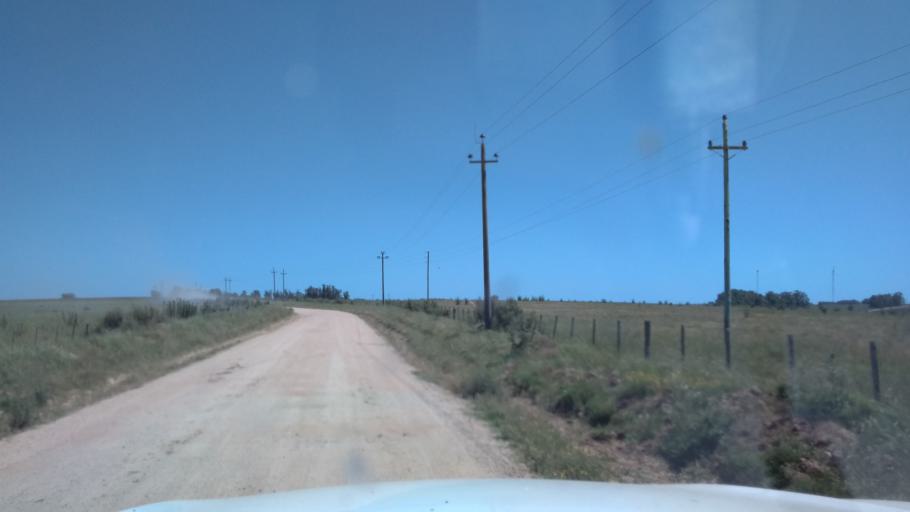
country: UY
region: Florida
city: Casupa
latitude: -34.0539
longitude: -55.8930
